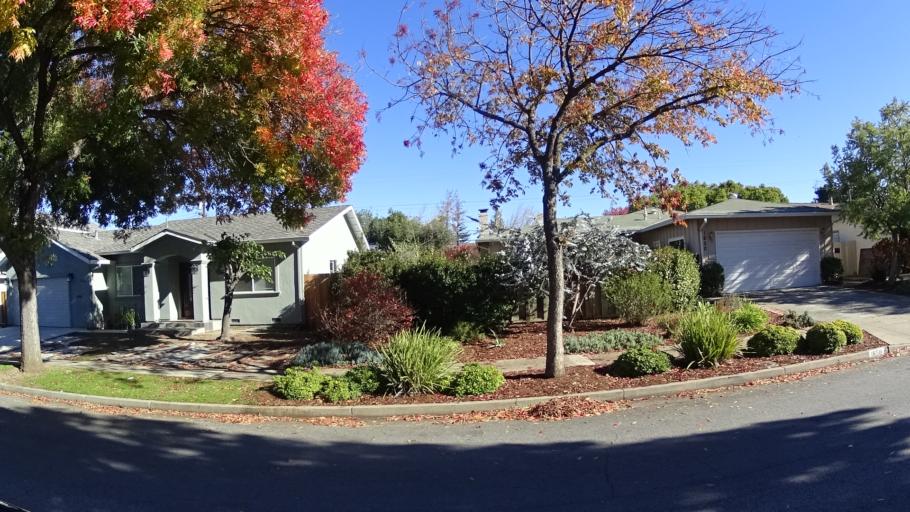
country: US
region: California
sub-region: Santa Clara County
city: Cupertino
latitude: 37.3395
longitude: -122.0193
